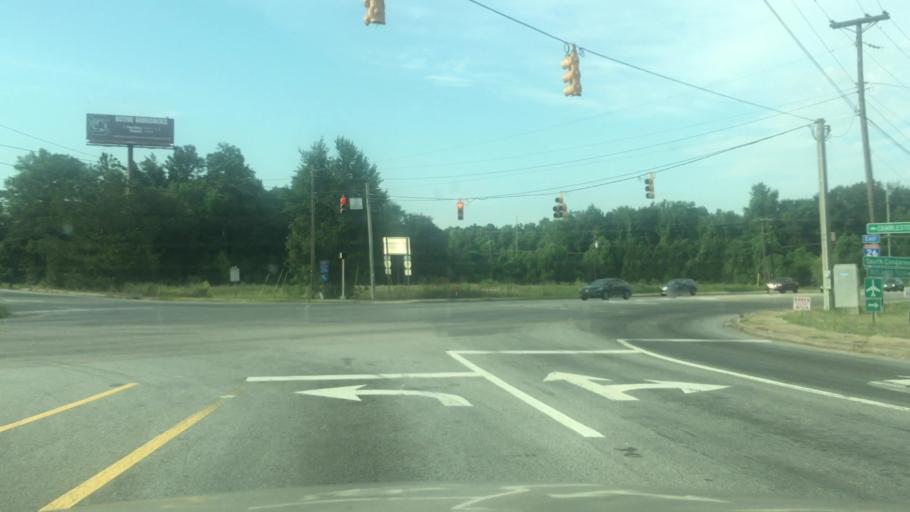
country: US
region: South Carolina
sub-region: Lexington County
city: Springdale
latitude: 33.9559
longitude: -81.0939
